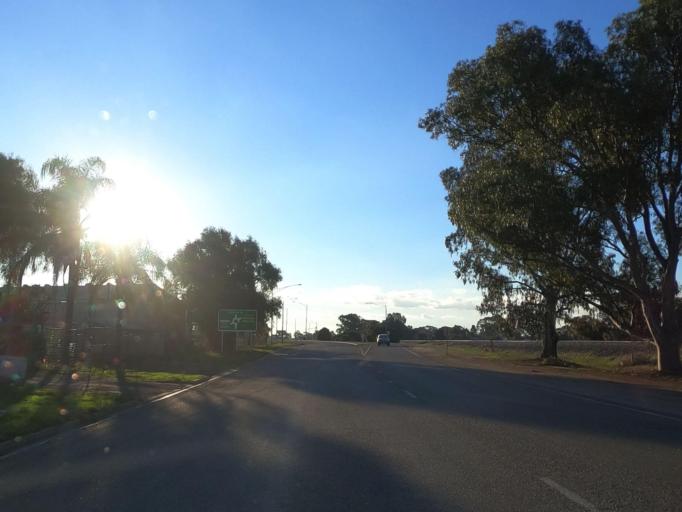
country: AU
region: Victoria
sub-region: Swan Hill
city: Swan Hill
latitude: -35.3287
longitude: 143.5548
